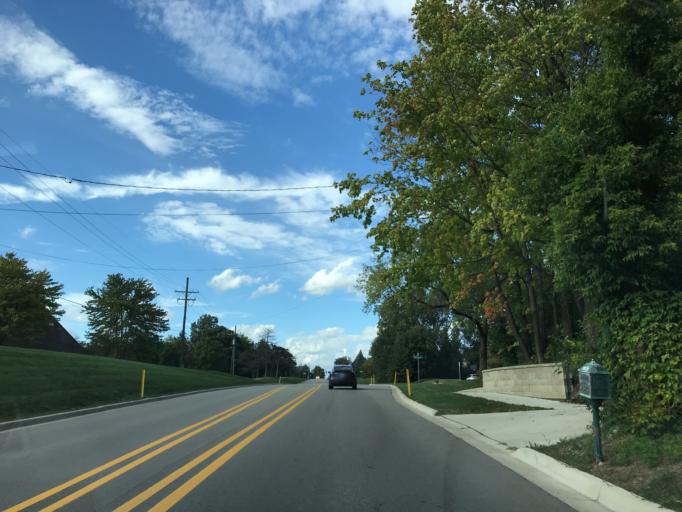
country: US
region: Michigan
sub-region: Oakland County
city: Farmington Hills
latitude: 42.5233
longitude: -83.3992
